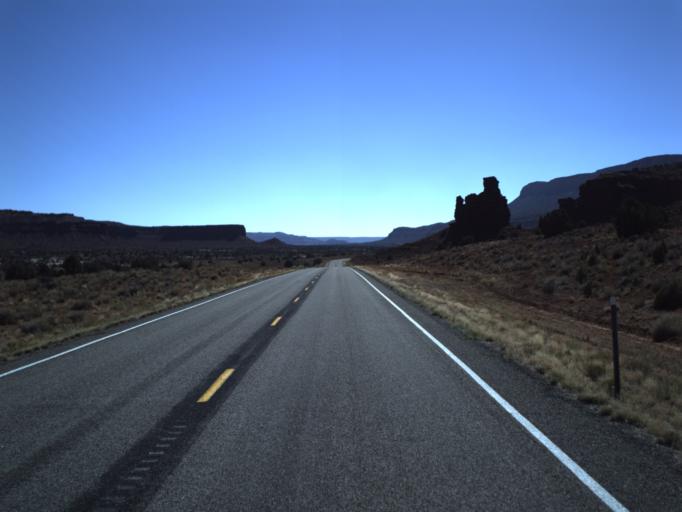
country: US
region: Utah
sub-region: San Juan County
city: Blanding
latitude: 37.7043
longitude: -110.2387
